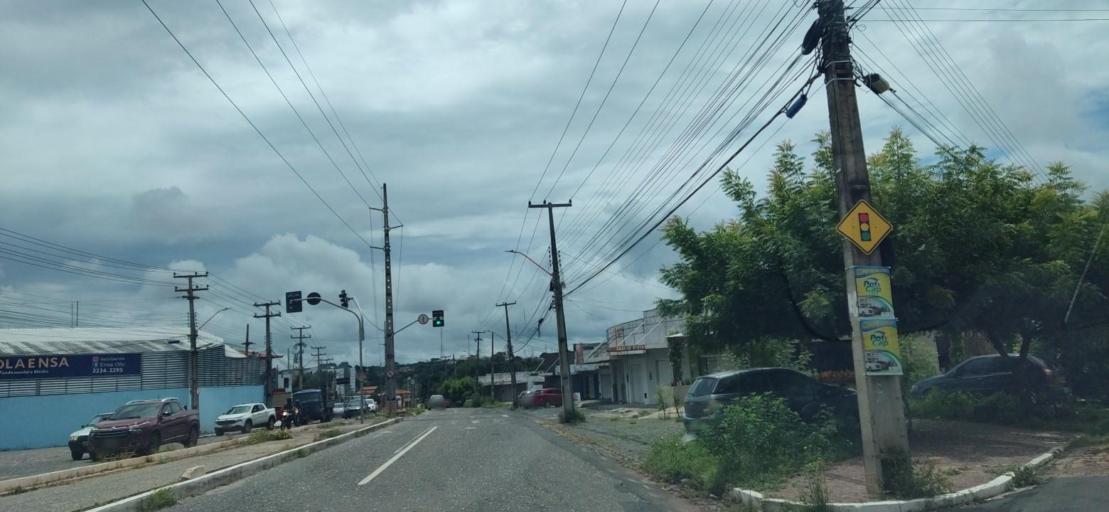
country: BR
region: Piaui
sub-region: Teresina
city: Teresina
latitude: -5.0622
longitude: -42.7573
